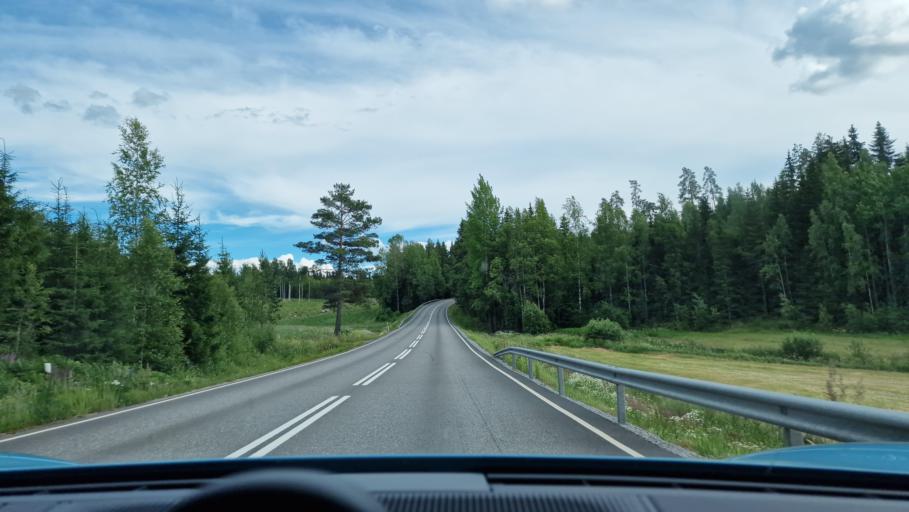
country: FI
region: Pirkanmaa
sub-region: Tampere
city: Orivesi
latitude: 61.5872
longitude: 24.3048
